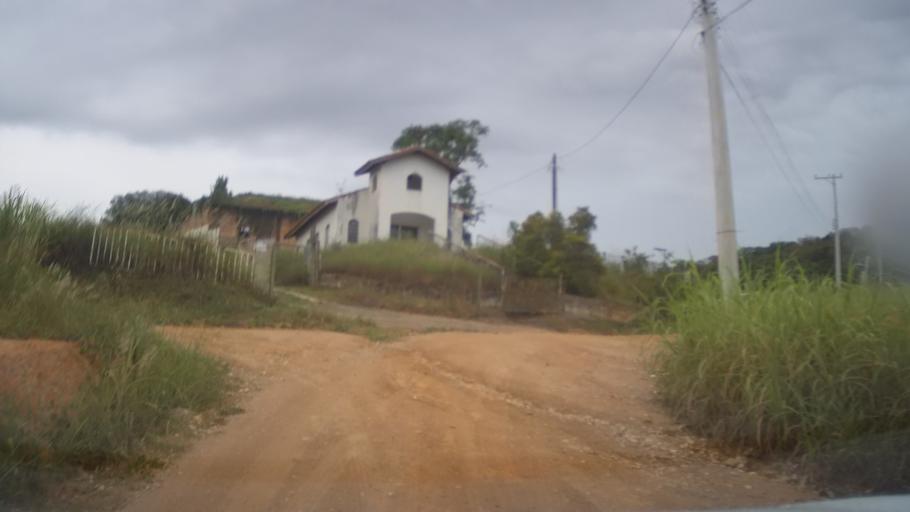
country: BR
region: Sao Paulo
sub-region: Itupeva
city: Itupeva
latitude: -23.1835
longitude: -47.0787
